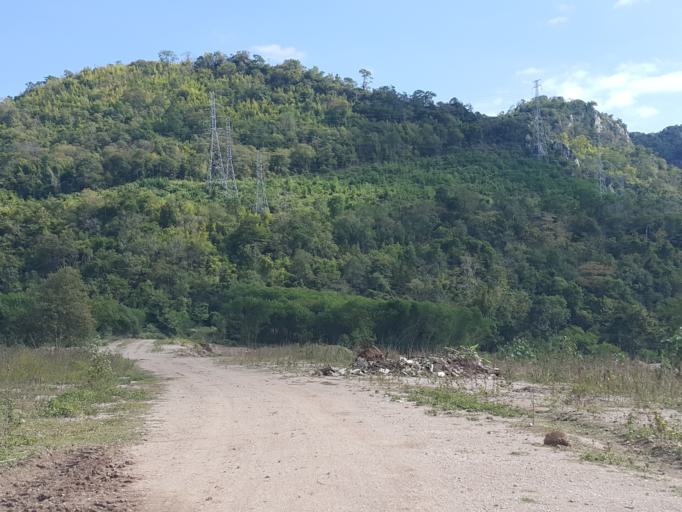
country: TH
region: Lampang
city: Mae Mo
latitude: 18.3278
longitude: 99.7616
